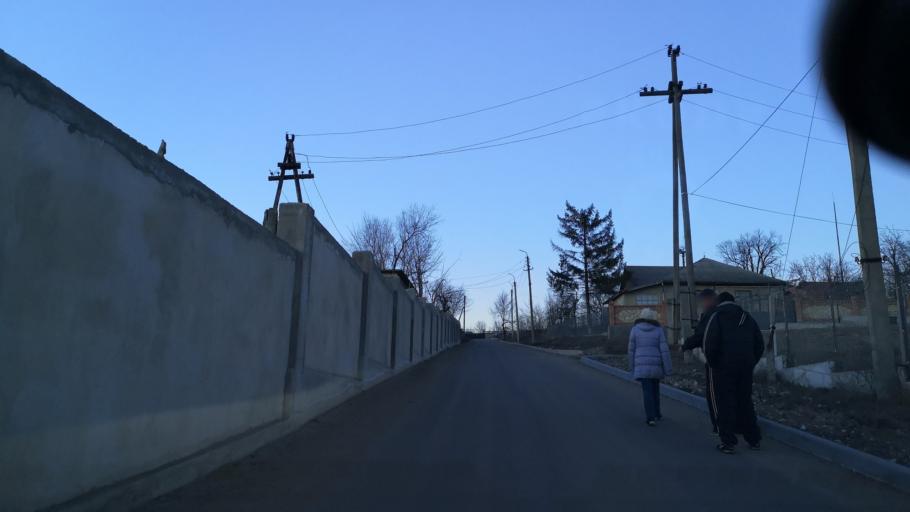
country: MD
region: Anenii Noi
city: Anenii Noi
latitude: 46.8925
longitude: 29.2930
